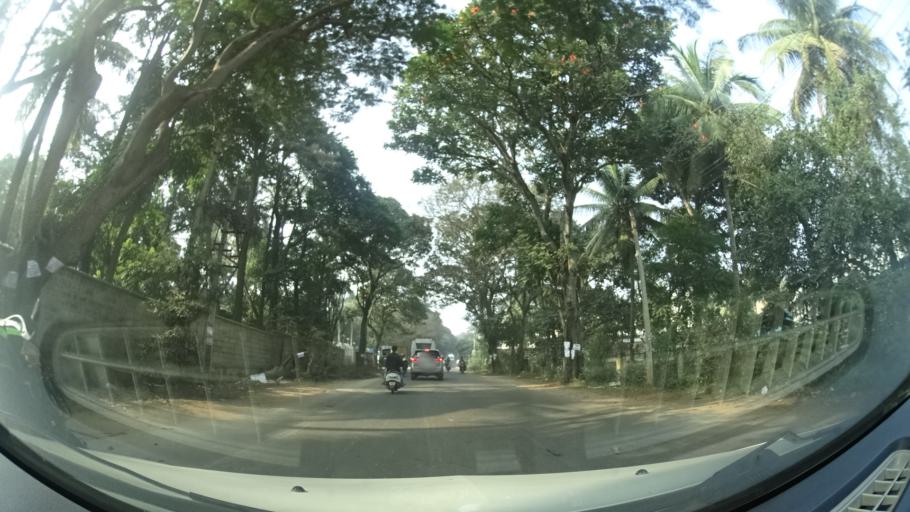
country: IN
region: Karnataka
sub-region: Bangalore Urban
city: Anekal
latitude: 12.8196
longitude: 77.6849
